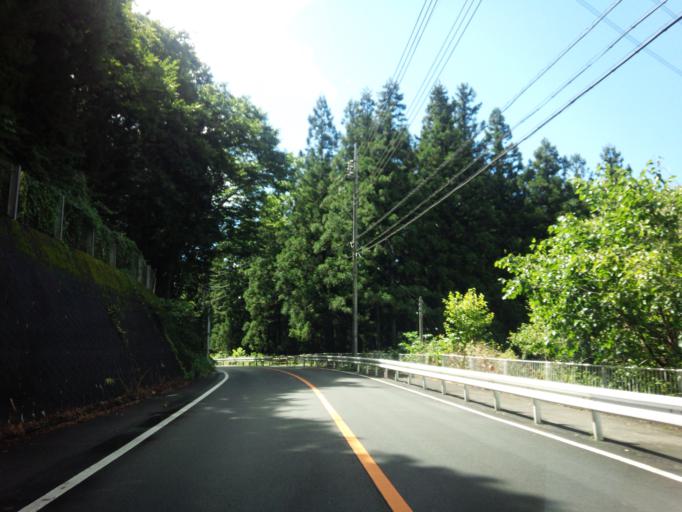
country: JP
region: Gunma
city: Nakanojomachi
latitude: 36.6198
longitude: 138.7952
